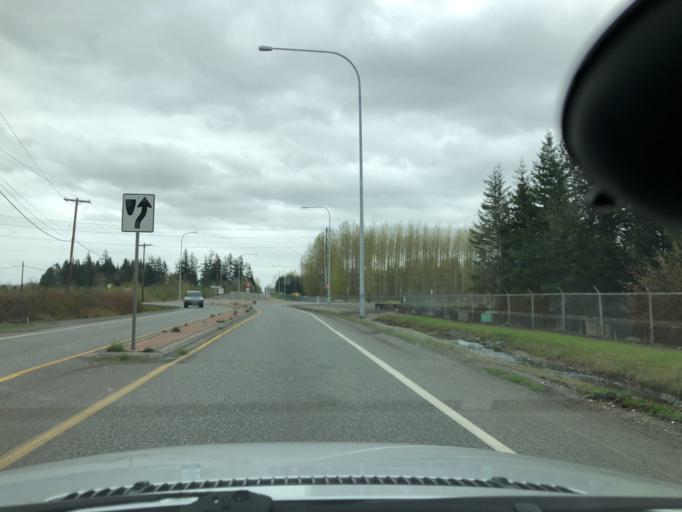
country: US
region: Washington
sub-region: Whatcom County
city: Birch Bay
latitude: 48.8920
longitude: -122.7282
